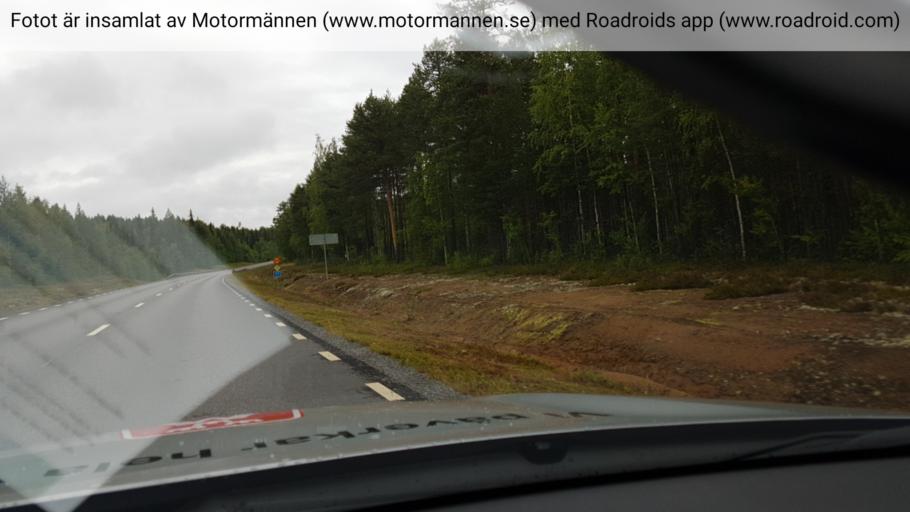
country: SE
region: Norrbotten
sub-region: Alvsbyns Kommun
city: AElvsbyn
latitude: 66.3374
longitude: 20.7502
